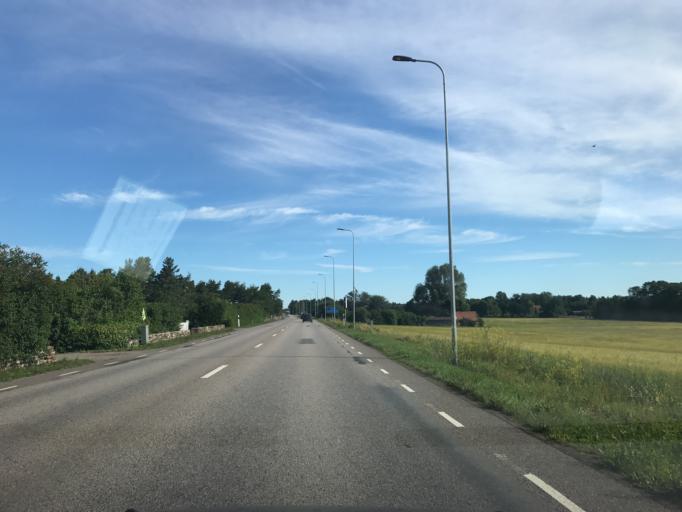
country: SE
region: Kalmar
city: Faerjestaden
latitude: 56.6876
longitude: 16.5220
